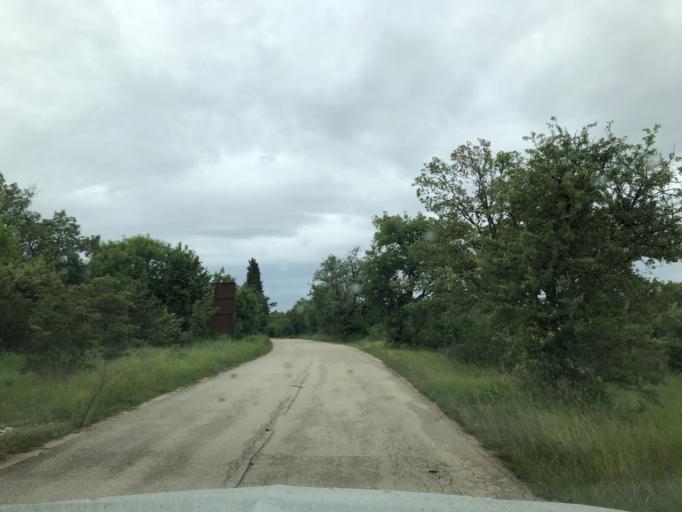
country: HR
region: Istarska
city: Buje
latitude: 45.4321
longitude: 13.6851
